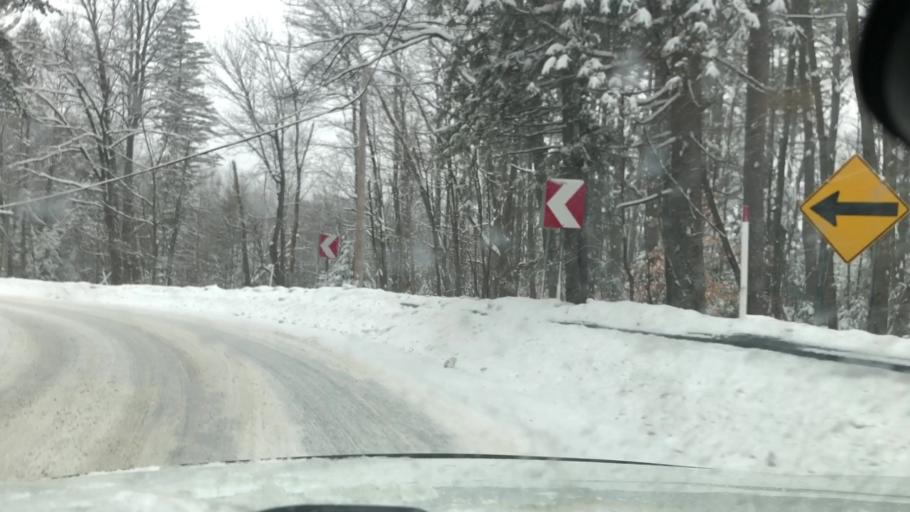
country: CA
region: Quebec
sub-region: Outaouais
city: Gatineau
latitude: 45.5153
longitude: -75.8398
